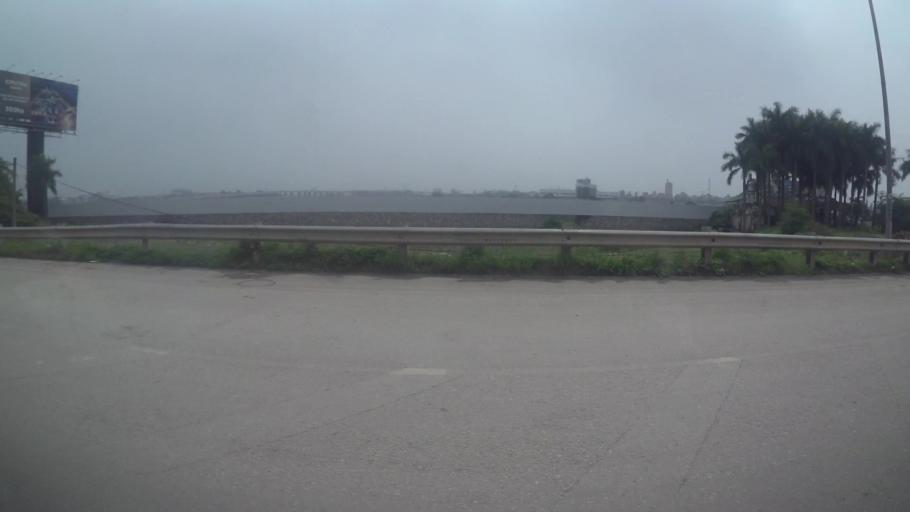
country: VN
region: Ha Noi
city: Tay Ho
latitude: 21.1222
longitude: 105.7826
